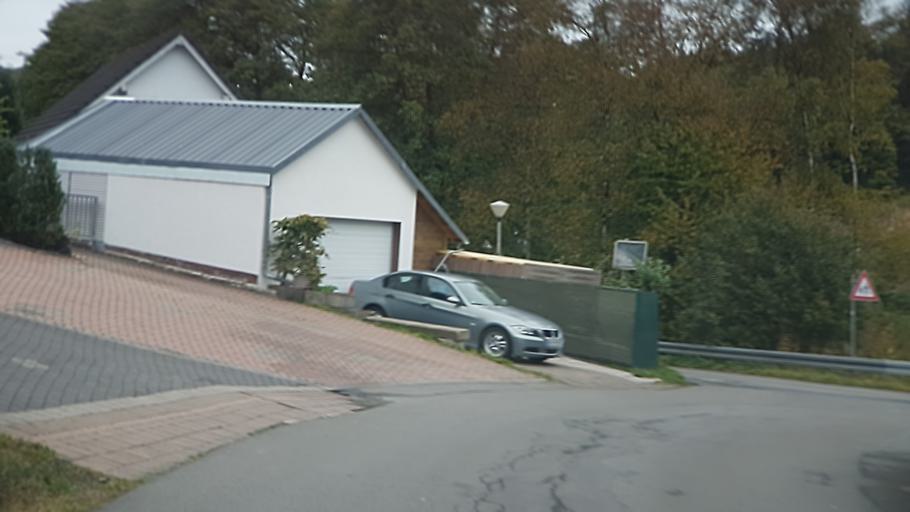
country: DE
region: North Rhine-Westphalia
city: Meinerzhagen
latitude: 51.1234
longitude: 7.6447
